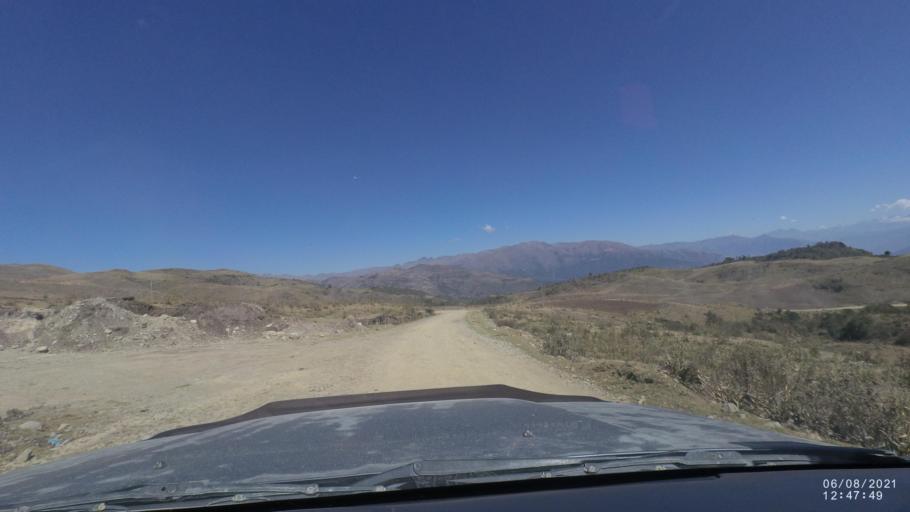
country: BO
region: Cochabamba
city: Colchani
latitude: -16.7587
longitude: -66.6710
